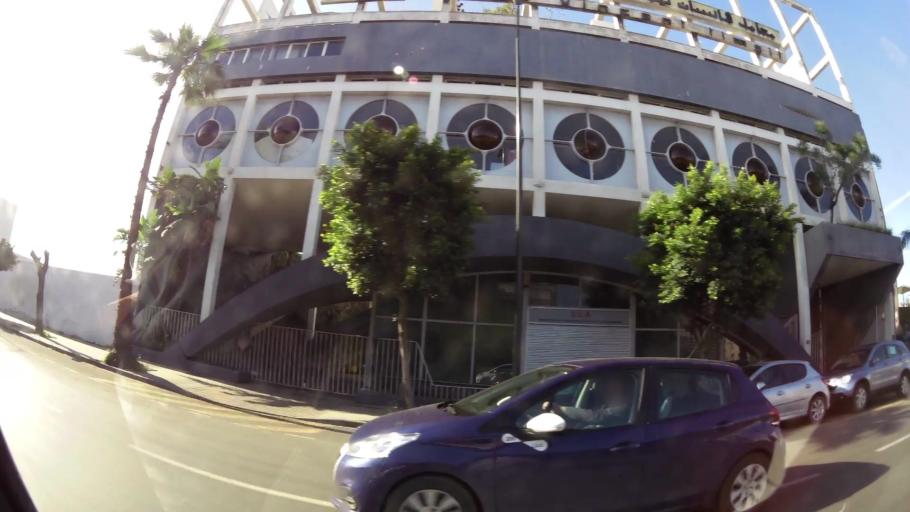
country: MA
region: Grand Casablanca
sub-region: Casablanca
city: Casablanca
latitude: 33.5984
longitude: -7.5785
